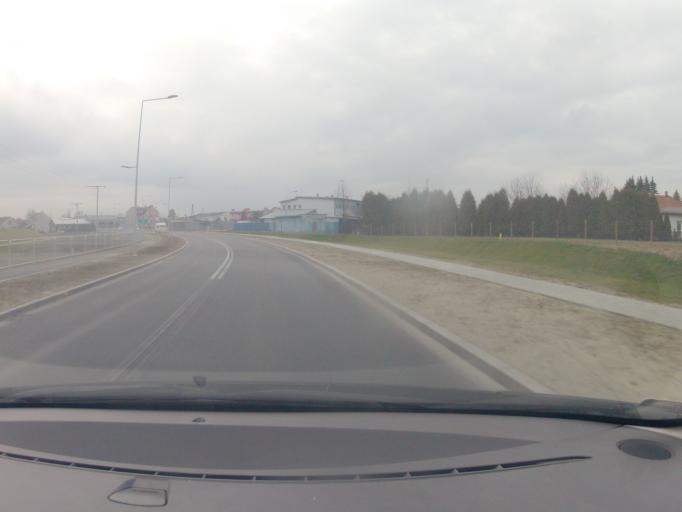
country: PL
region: Subcarpathian Voivodeship
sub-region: Powiat jasielski
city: Jaslo
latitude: 49.7510
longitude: 21.4775
